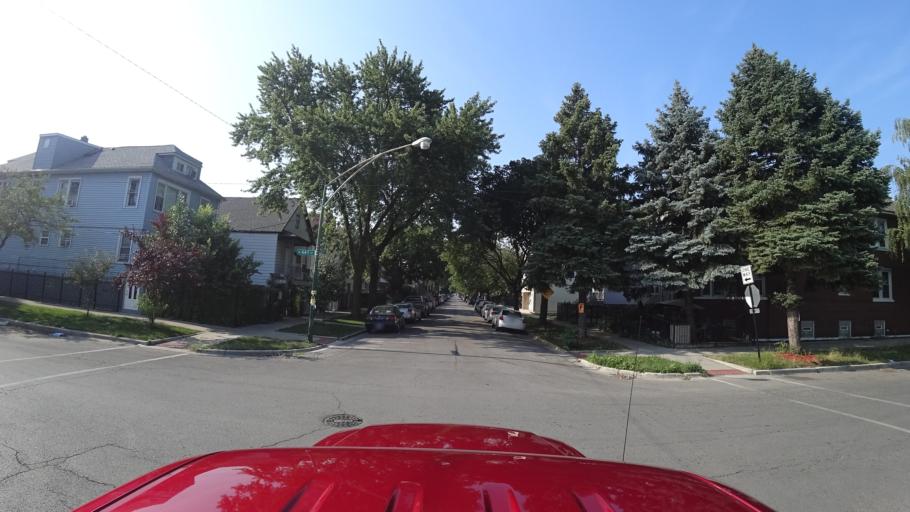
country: US
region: Illinois
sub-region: Cook County
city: Chicago
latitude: 41.8138
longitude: -87.6956
